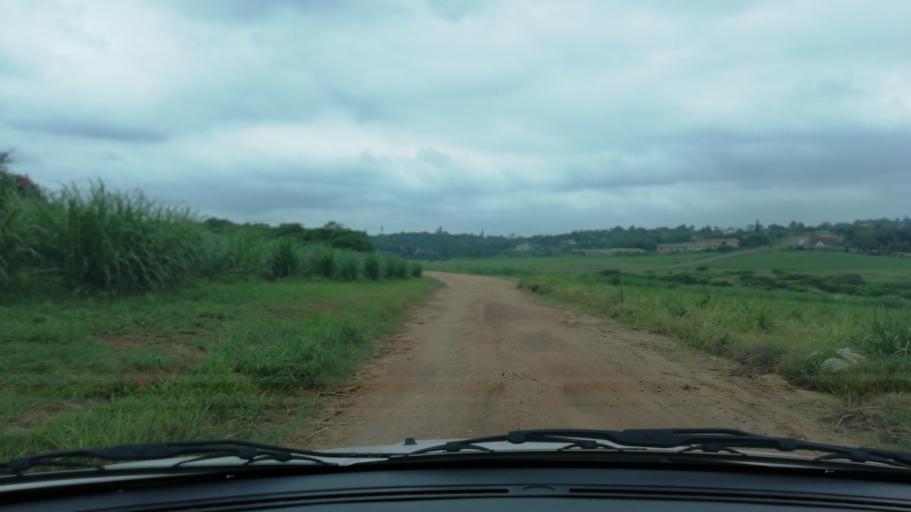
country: ZA
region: KwaZulu-Natal
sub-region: uThungulu District Municipality
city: Empangeni
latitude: -28.7359
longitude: 31.9076
